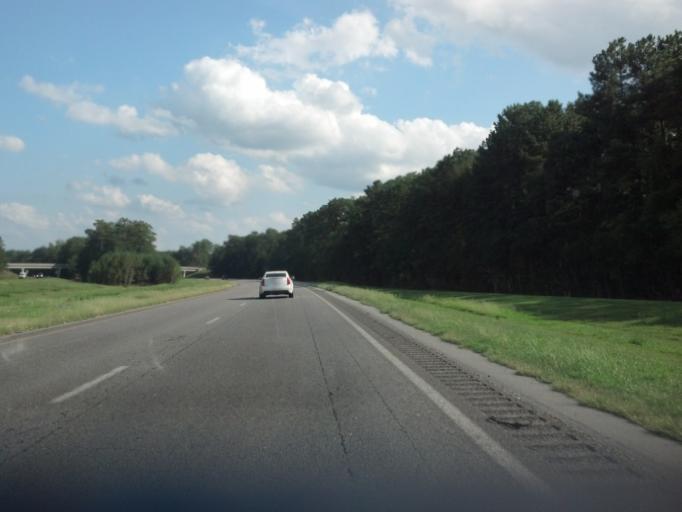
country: US
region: North Carolina
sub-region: Nash County
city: Rocky Mount
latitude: 35.9437
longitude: -77.7586
